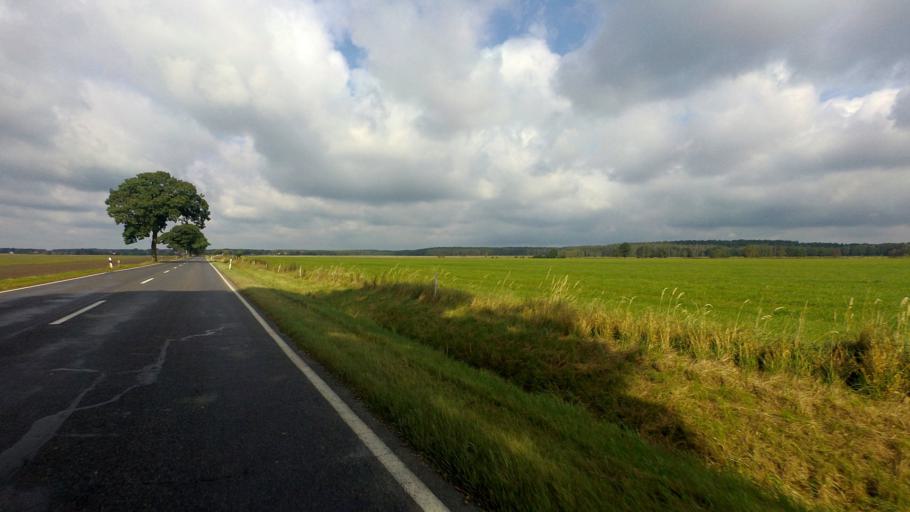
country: DE
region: Saxony
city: Wiednitz
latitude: 51.3926
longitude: 14.0182
